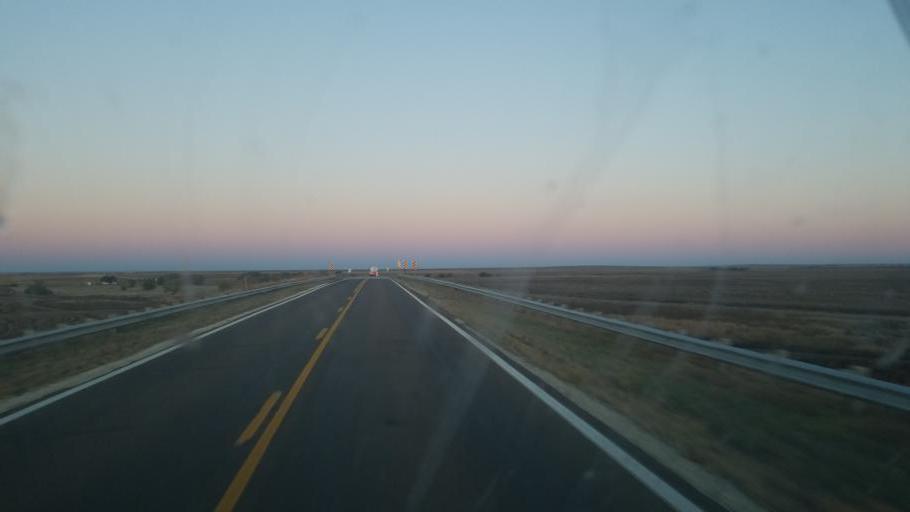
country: US
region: Kansas
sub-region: Wallace County
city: Sharon Springs
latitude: 38.9055
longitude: -101.6166
